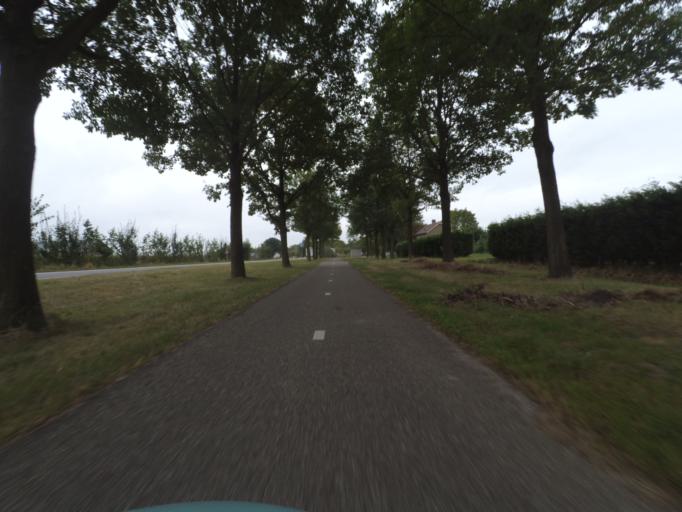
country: NL
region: Gelderland
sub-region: Gemeente Geldermalsen
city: Geldermalsen
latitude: 51.9193
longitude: 5.3290
